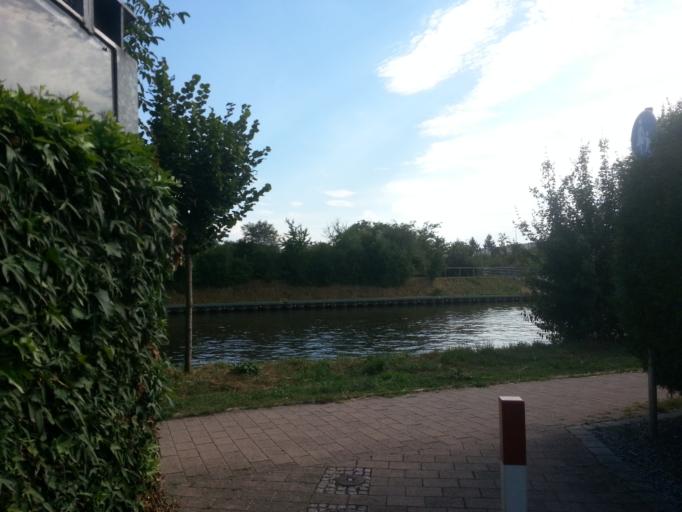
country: DE
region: Baden-Wuerttemberg
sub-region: Karlsruhe Region
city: Ilvesheim
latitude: 49.4791
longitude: 8.5590
